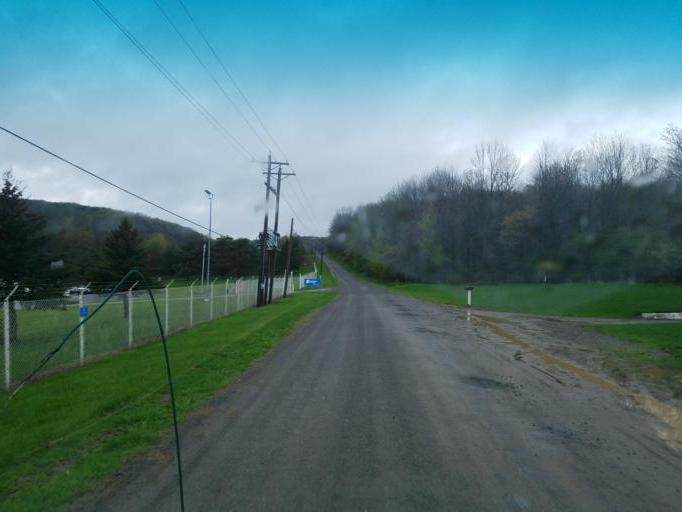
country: US
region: Pennsylvania
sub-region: Tioga County
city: Westfield
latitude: 41.9802
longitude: -77.6871
